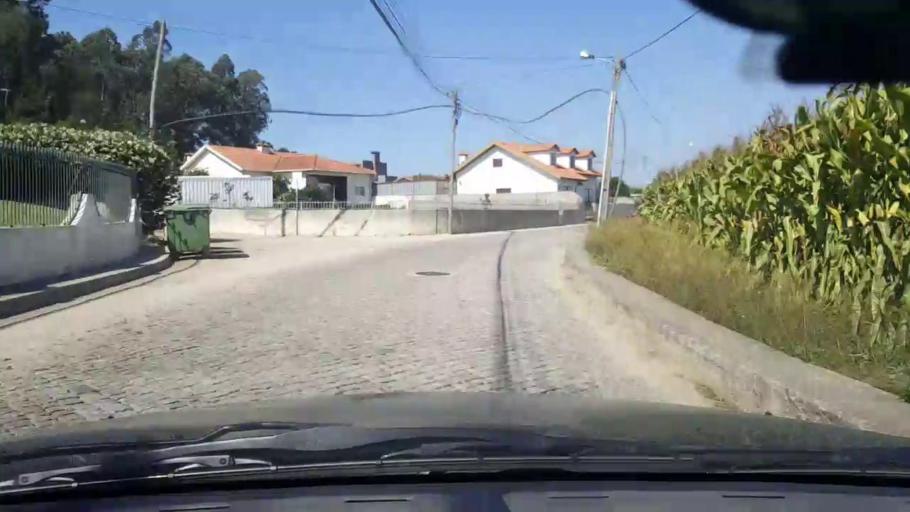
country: PT
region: Porto
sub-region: Matosinhos
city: Lavra
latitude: 41.2629
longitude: -8.6959
